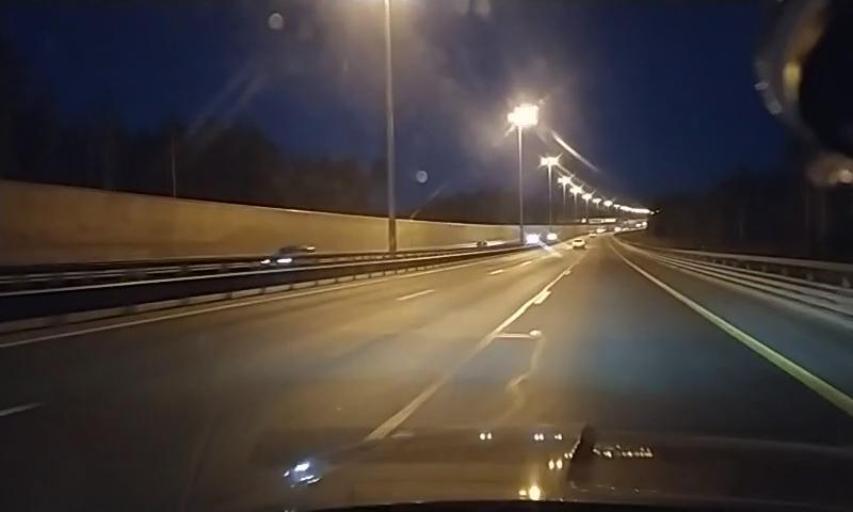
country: RU
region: St.-Petersburg
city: Beloostrov
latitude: 60.1162
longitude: 30.0774
